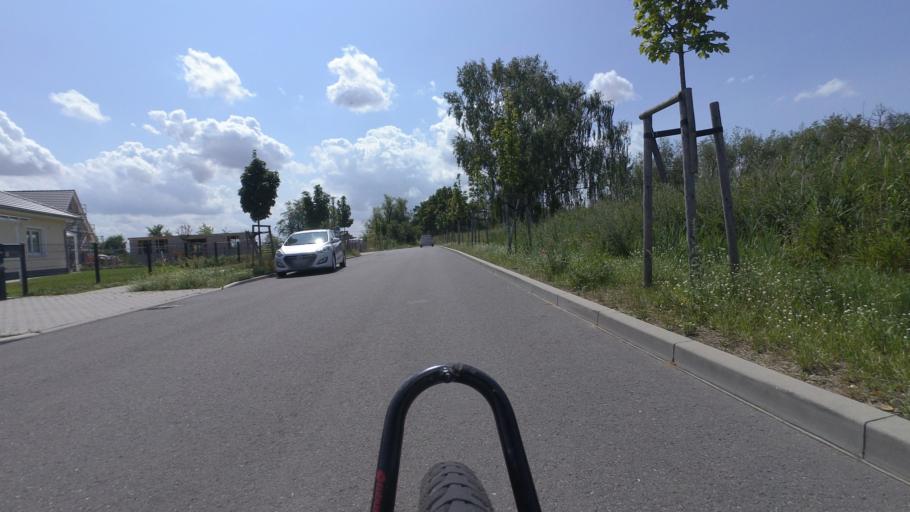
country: DE
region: Brandenburg
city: Grossbeeren
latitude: 52.3492
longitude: 13.2985
